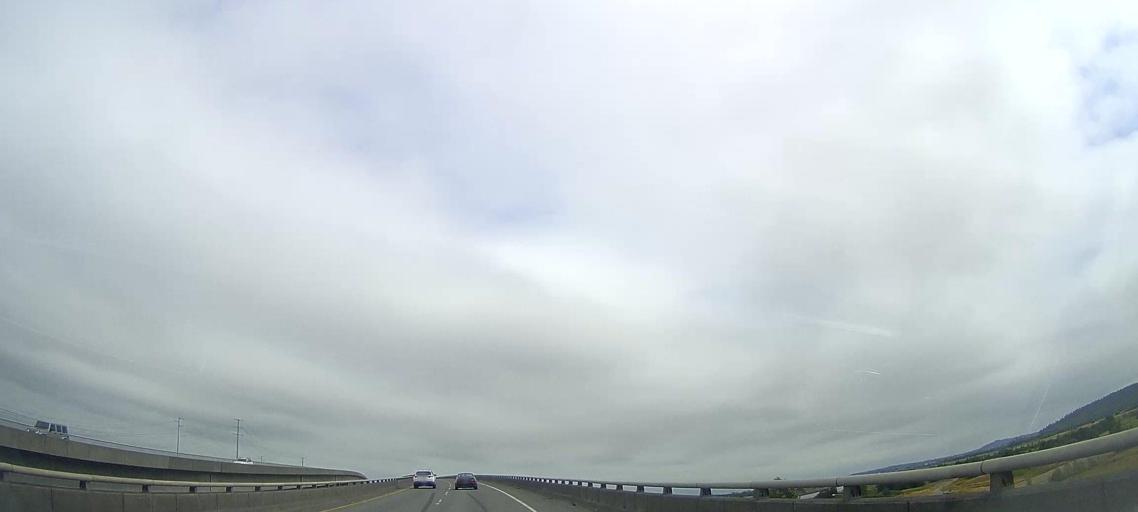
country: US
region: Washington
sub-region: Skagit County
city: Anacortes
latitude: 48.4550
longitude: -122.5223
